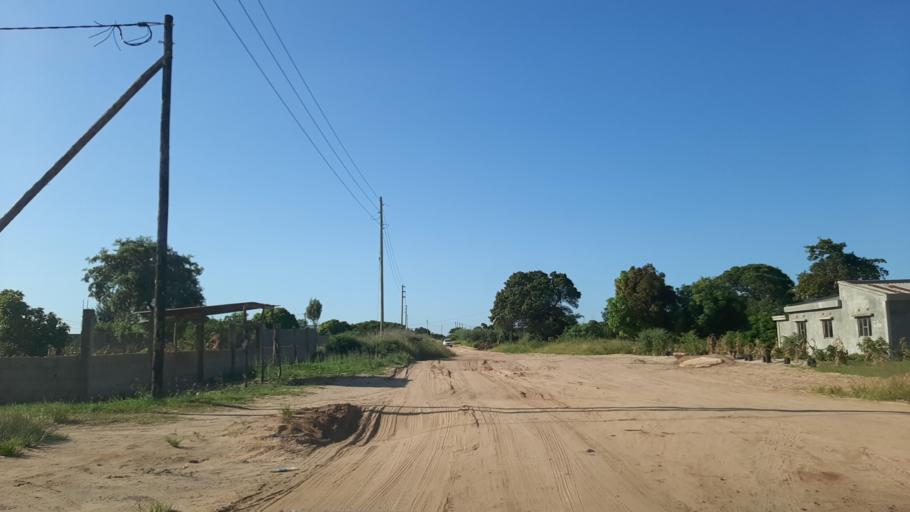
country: MZ
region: Maputo City
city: Maputo
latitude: -25.7577
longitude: 32.5504
